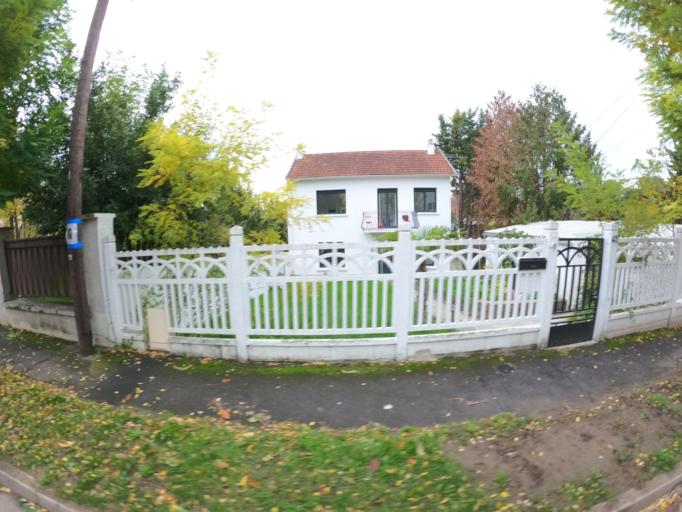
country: FR
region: Ile-de-France
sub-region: Departement du Val-de-Marne
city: Sucy-en-Brie
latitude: 48.7799
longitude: 2.5162
